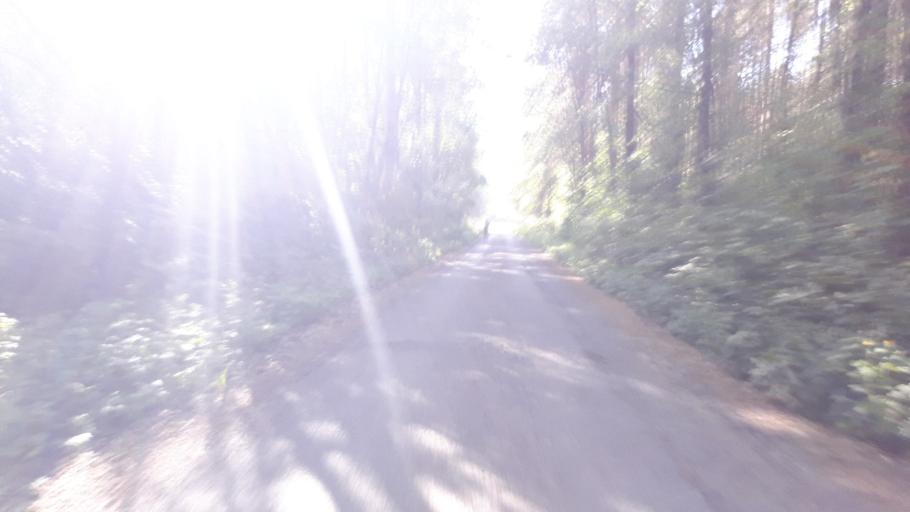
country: EE
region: Harju
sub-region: Tallinna linn
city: Kose
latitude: 59.4497
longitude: 24.9030
